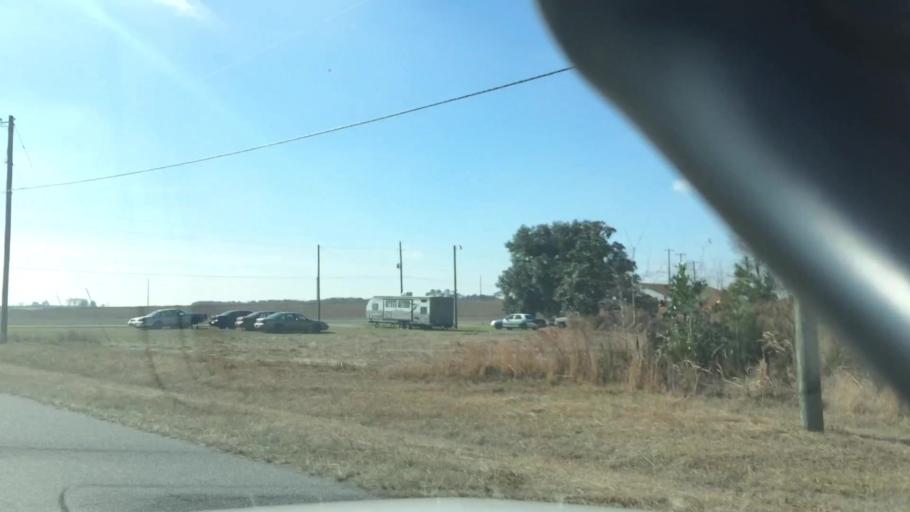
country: US
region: North Carolina
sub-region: Pitt County
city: Ayden
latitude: 35.4677
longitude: -77.4392
